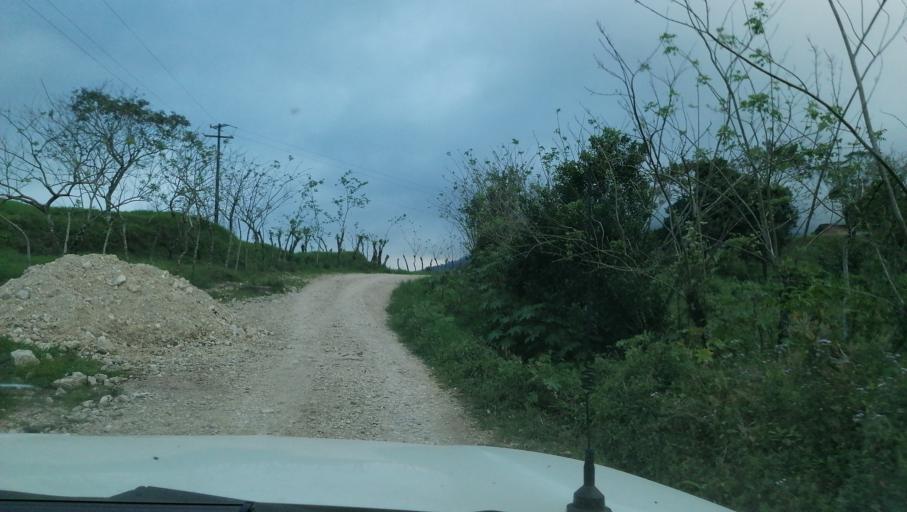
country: MX
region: Chiapas
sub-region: Francisco Leon
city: San Miguel la Sardina
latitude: 17.2880
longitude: -93.2699
